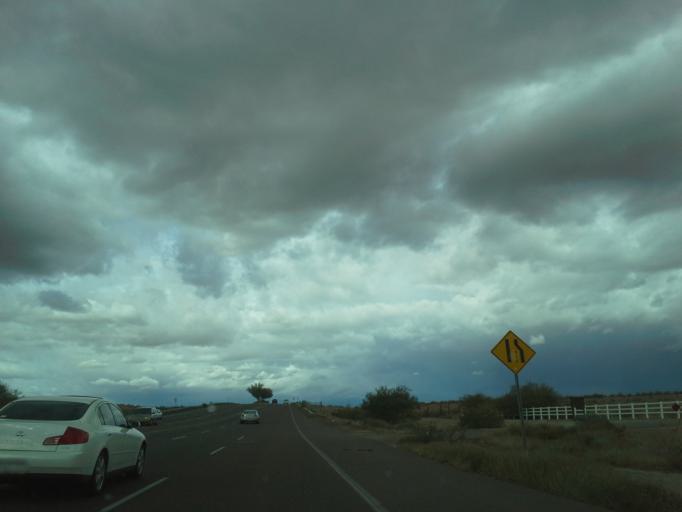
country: US
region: Arizona
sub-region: Maricopa County
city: Paradise Valley
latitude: 33.6565
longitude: -111.9773
